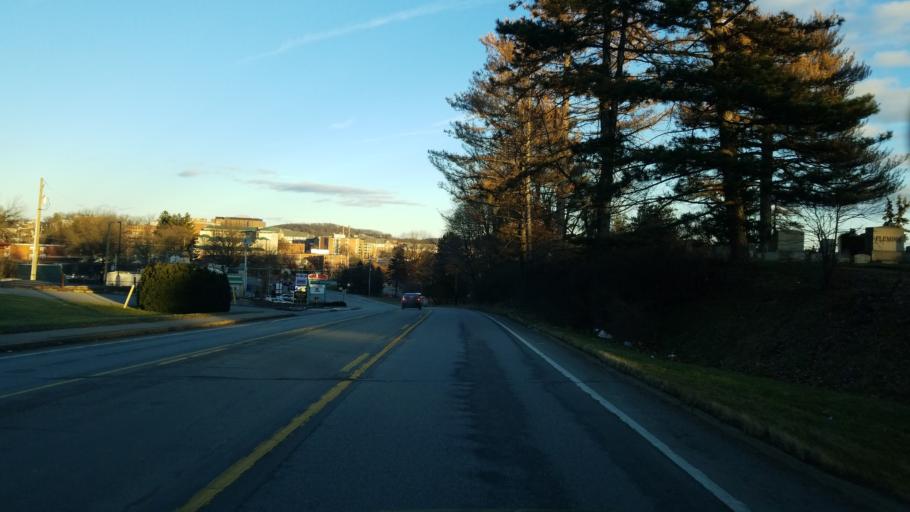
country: US
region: Pennsylvania
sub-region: Indiana County
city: Indiana
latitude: 40.6150
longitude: -79.1696
